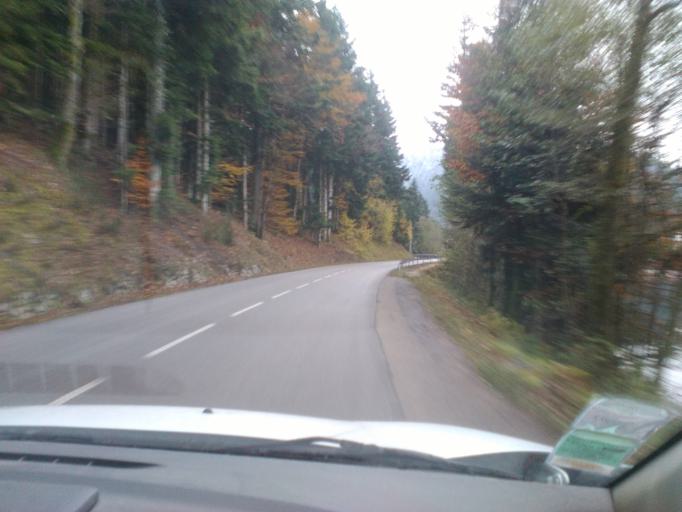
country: FR
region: Lorraine
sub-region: Departement des Vosges
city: Xonrupt-Longemer
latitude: 48.0761
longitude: 6.9507
